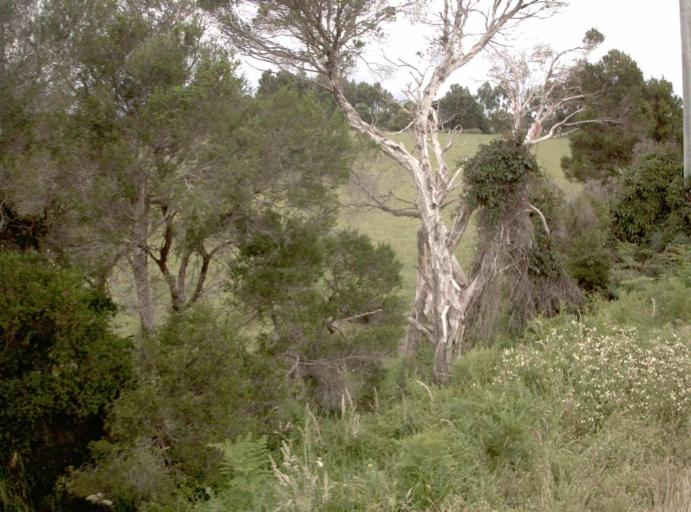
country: AU
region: Victoria
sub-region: Bass Coast
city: North Wonthaggi
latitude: -38.5507
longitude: 145.6708
